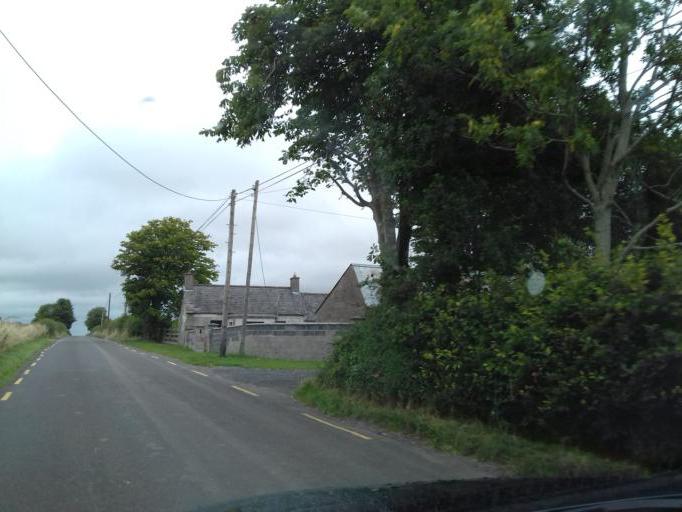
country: IE
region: Leinster
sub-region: County Carlow
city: Bagenalstown
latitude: 52.6185
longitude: -7.0370
